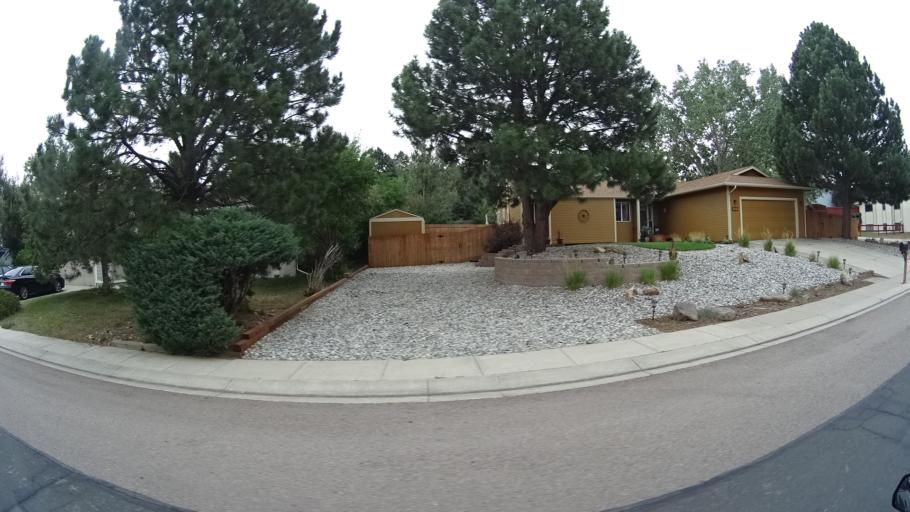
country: US
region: Colorado
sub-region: El Paso County
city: Air Force Academy
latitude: 38.9232
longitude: -104.8119
